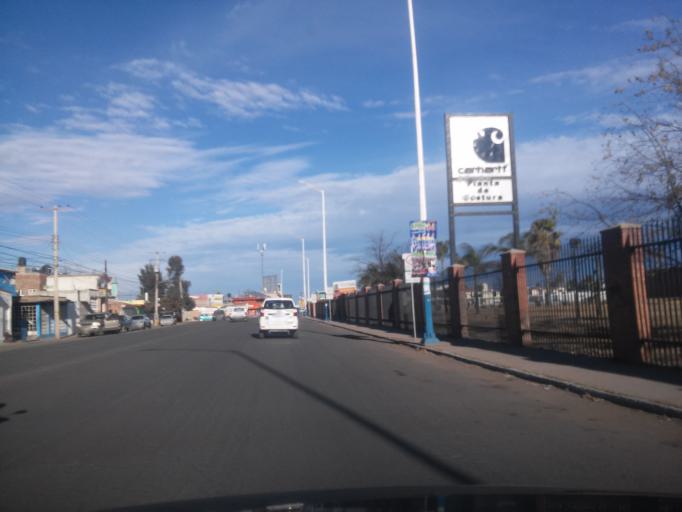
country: MX
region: Durango
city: Victoria de Durango
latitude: 24.0057
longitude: -104.6461
